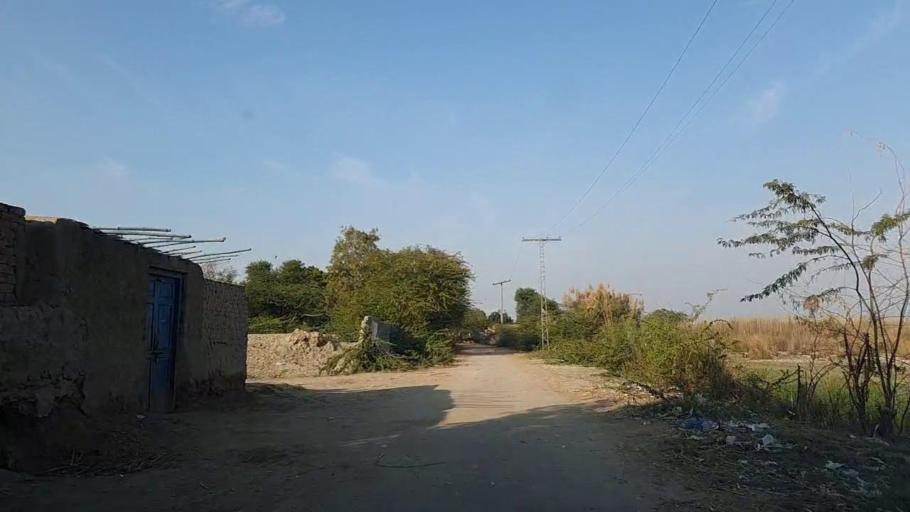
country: PK
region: Sindh
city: Nawabshah
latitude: 26.3825
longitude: 68.4851
